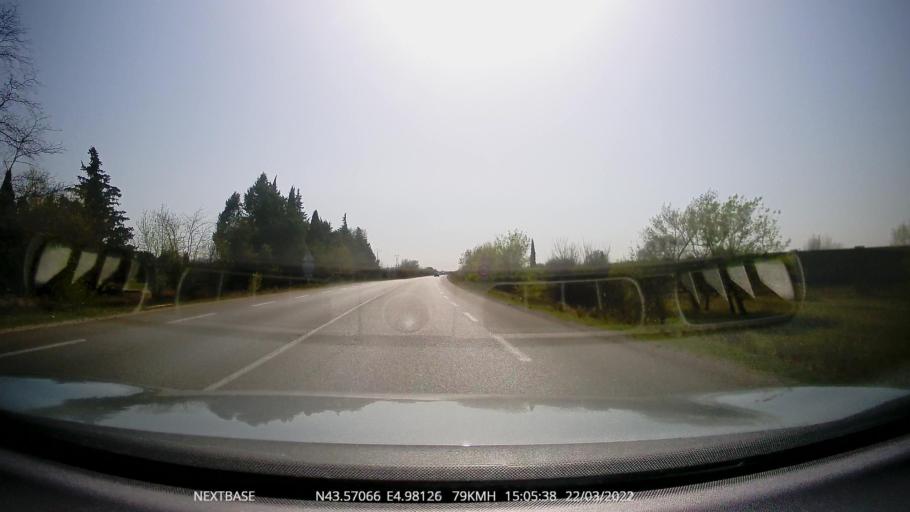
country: FR
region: Provence-Alpes-Cote d'Azur
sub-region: Departement des Bouches-du-Rhone
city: Miramas
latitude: 43.5708
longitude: 4.9819
